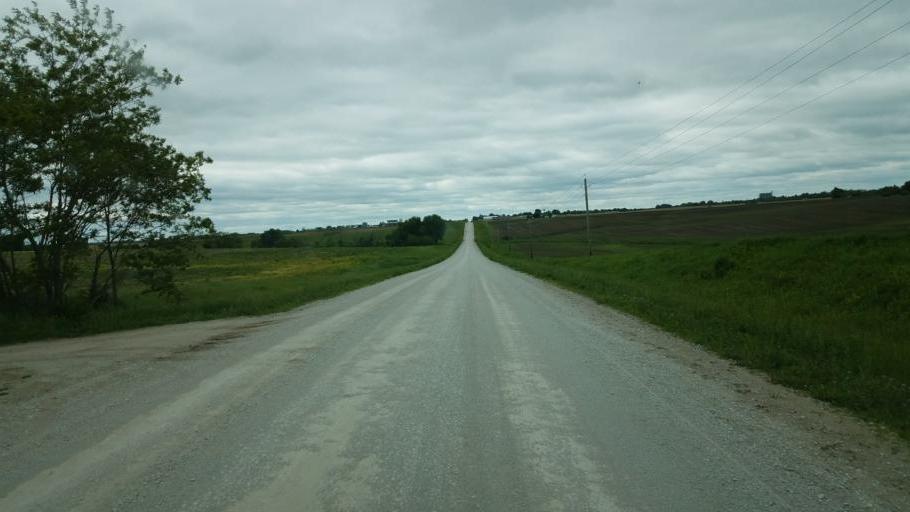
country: US
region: Iowa
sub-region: Decatur County
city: Lamoni
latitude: 40.6456
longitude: -93.9201
